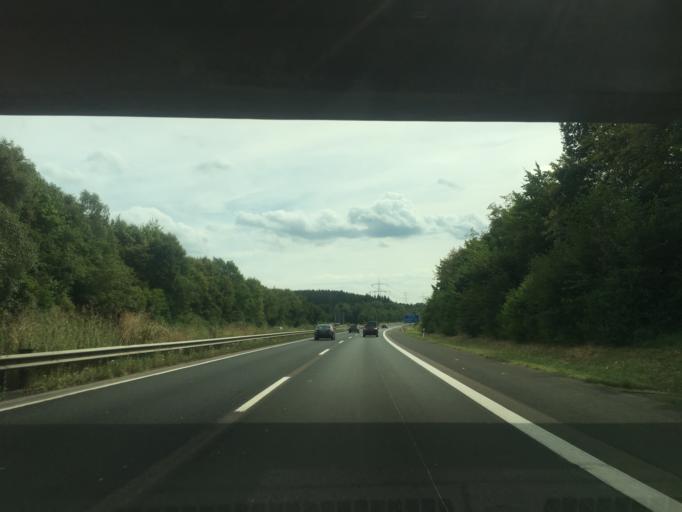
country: DE
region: Rheinland-Pfalz
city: Wiebelsheim
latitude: 50.0714
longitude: 7.6283
